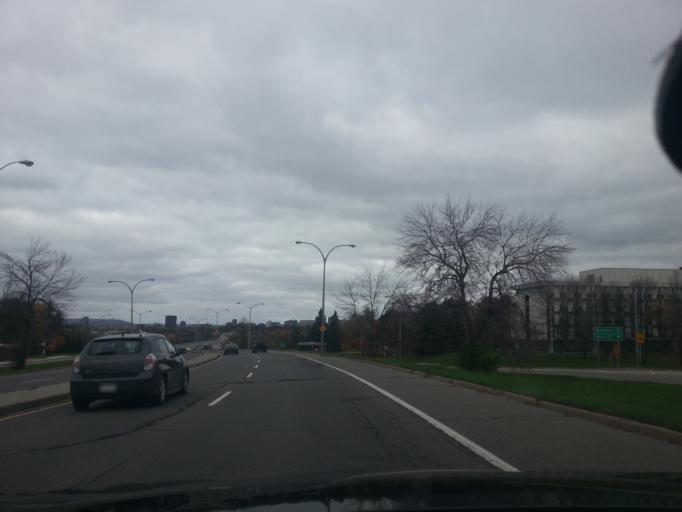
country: CA
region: Ontario
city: Ottawa
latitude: 45.3784
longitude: -75.6844
